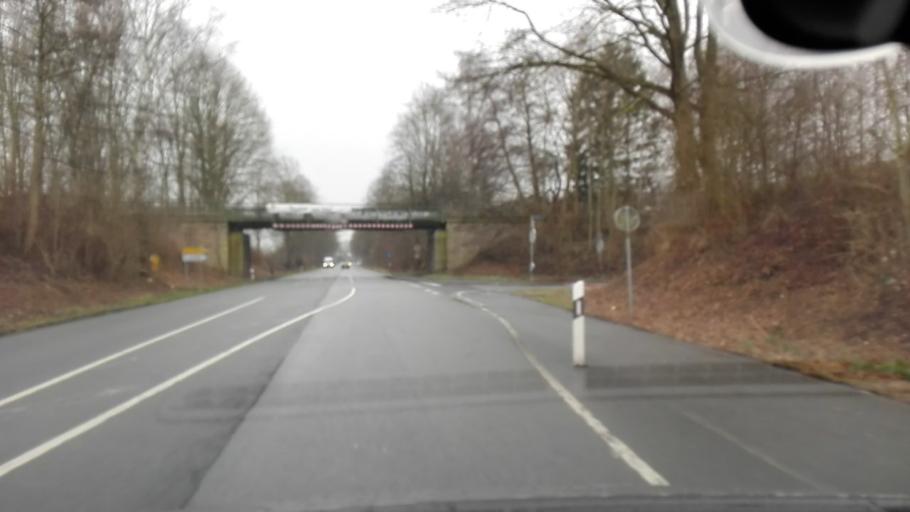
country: DE
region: North Rhine-Westphalia
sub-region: Regierungsbezirk Arnsberg
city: Unna
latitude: 51.5739
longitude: 7.7199
